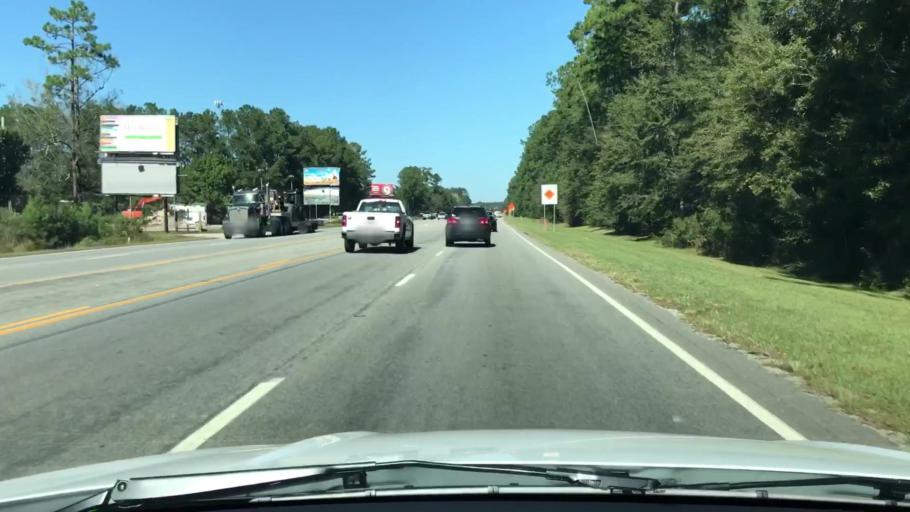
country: US
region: South Carolina
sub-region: Beaufort County
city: Bluffton
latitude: 32.3053
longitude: -80.9350
